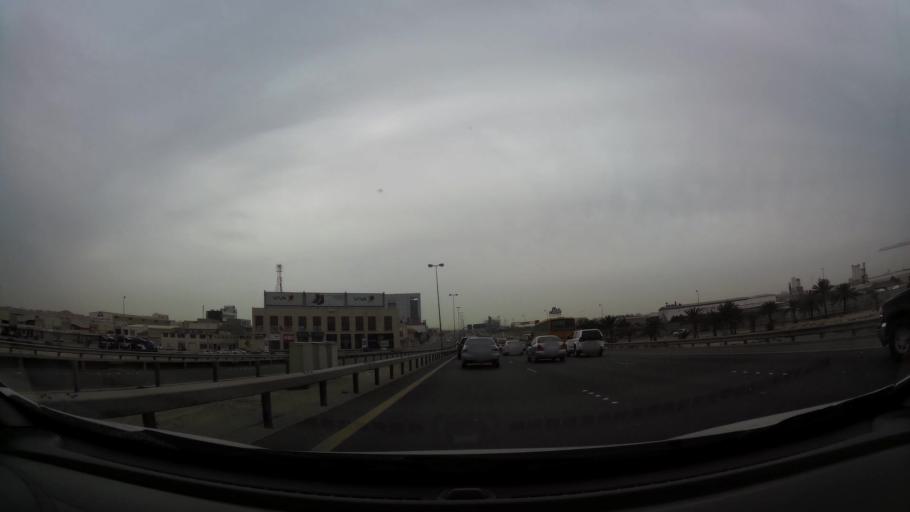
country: BH
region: Northern
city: Madinat `Isa
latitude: 26.1937
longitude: 50.5350
